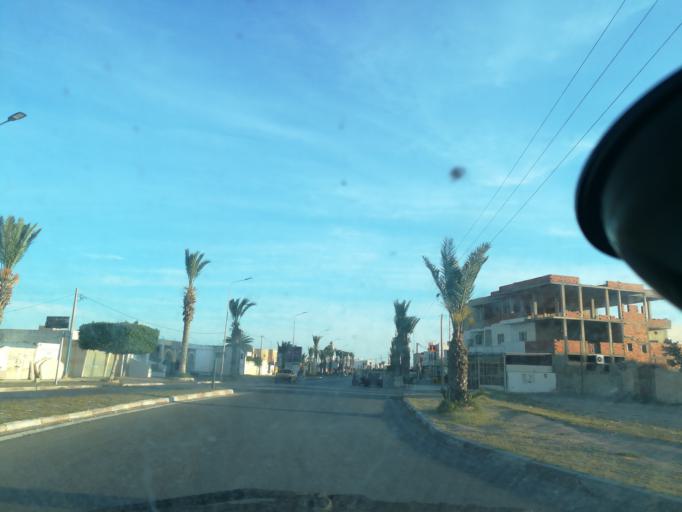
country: TN
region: Safaqis
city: Al Qarmadah
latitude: 34.8249
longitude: 10.7634
